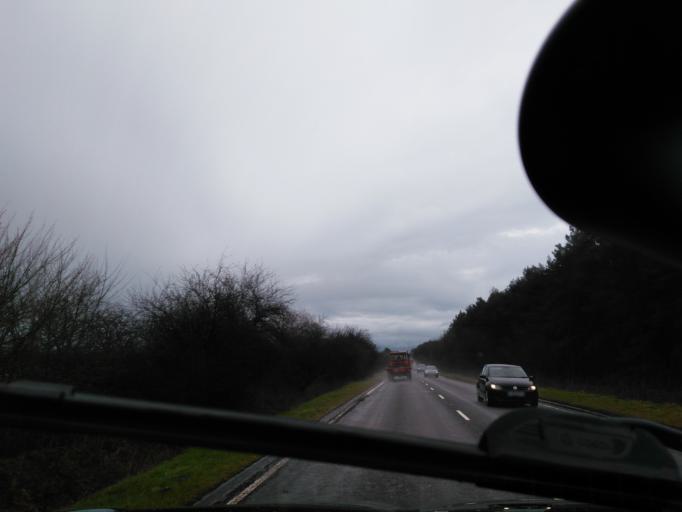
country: GB
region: England
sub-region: City and Borough of Leeds
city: Otley
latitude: 53.9999
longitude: -1.6857
